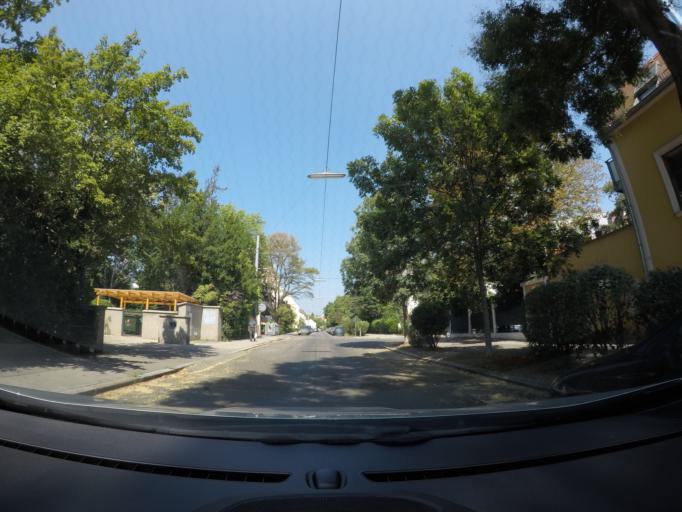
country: AT
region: Lower Austria
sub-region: Politischer Bezirk Modling
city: Perchtoldsdorf
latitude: 48.1890
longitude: 16.2721
